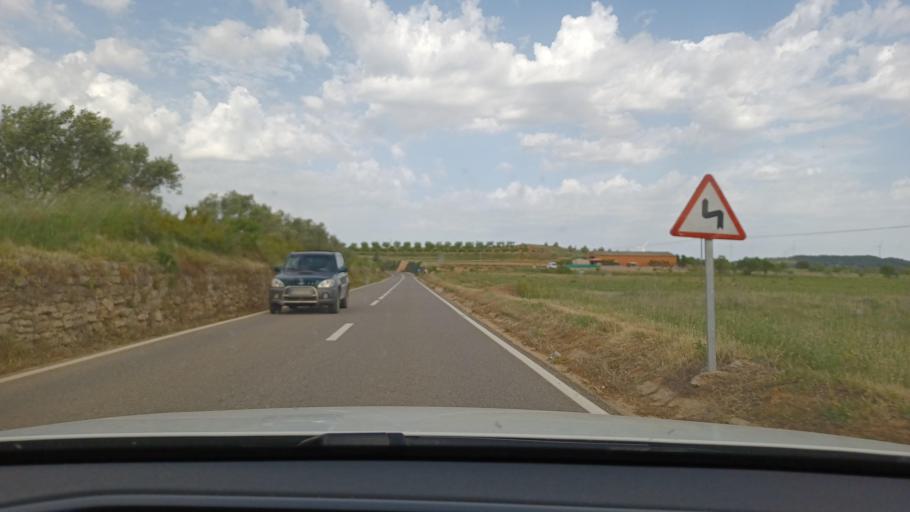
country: ES
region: Catalonia
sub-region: Provincia de Tarragona
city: Gandesa
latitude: 41.0513
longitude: 0.4333
